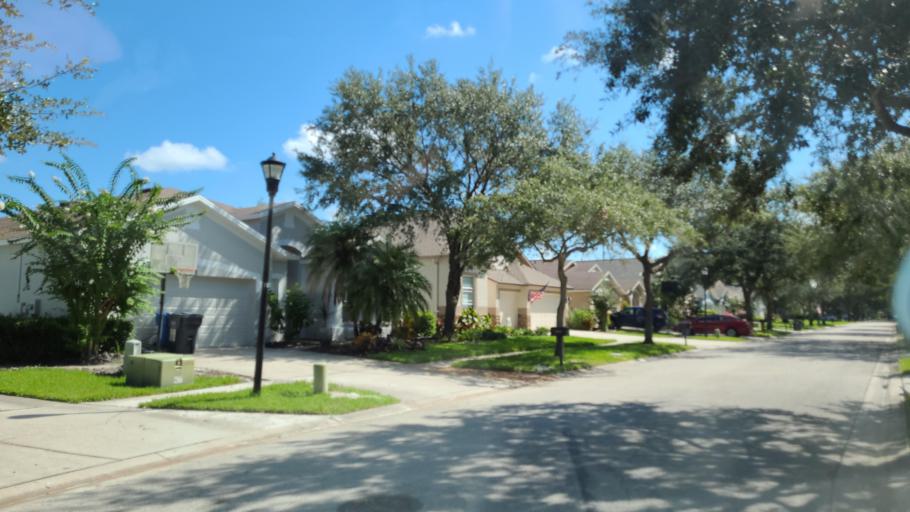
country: US
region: Florida
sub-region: Hillsborough County
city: Fish Hawk
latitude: 27.8401
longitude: -82.2302
